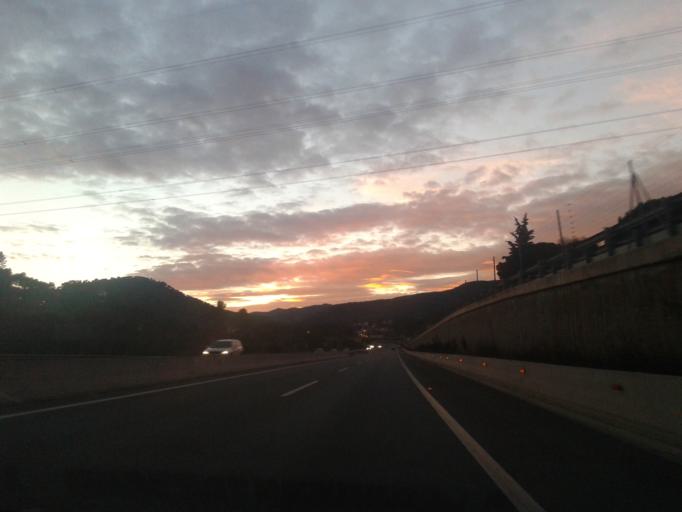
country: ES
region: Catalonia
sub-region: Provincia de Barcelona
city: Cervello
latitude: 41.3992
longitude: 1.9805
